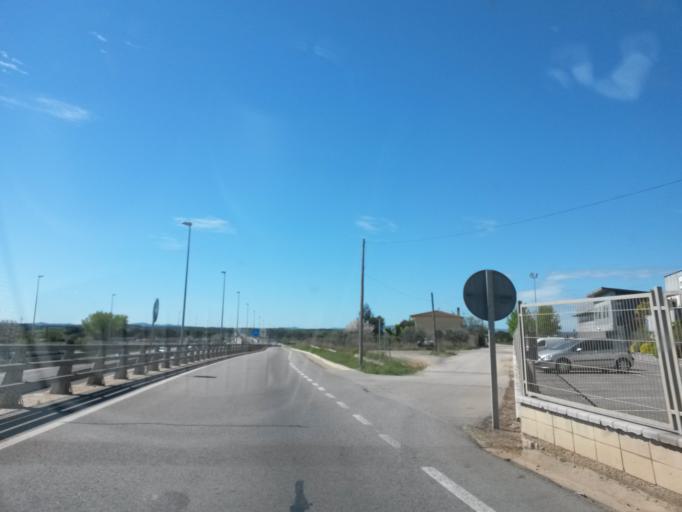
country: ES
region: Catalonia
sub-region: Provincia de Girona
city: Riudellots de la Selva
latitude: 41.9003
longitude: 2.7864
